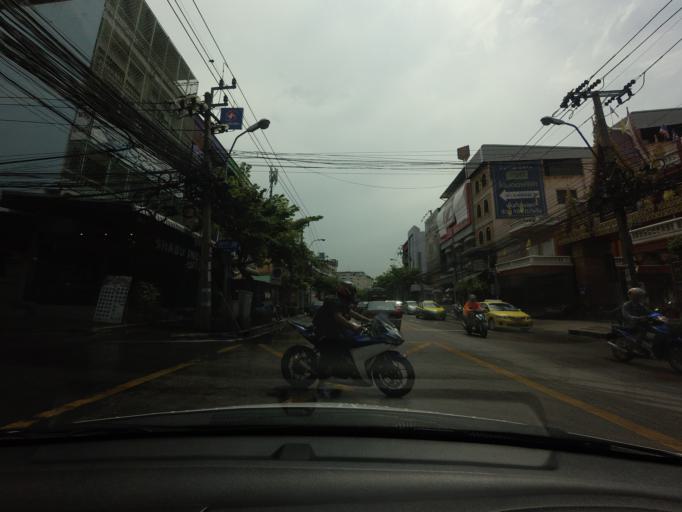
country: TH
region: Bangkok
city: Phra Khanong
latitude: 13.7089
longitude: 100.6179
